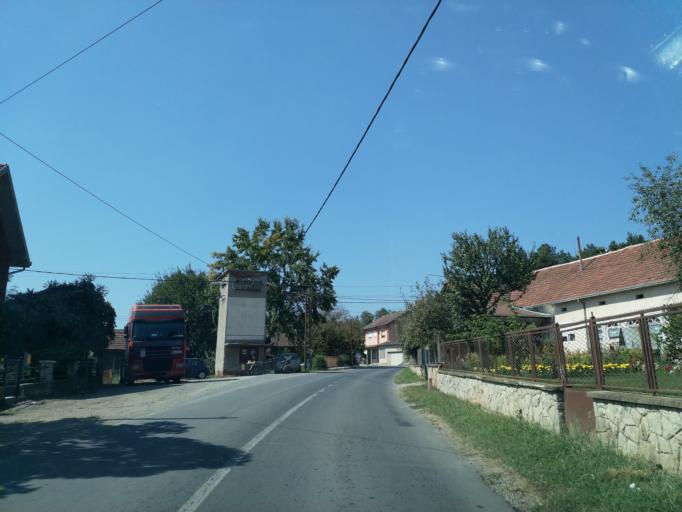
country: RS
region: Central Serbia
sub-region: Rasinski Okrug
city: Krusevac
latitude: 43.6150
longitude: 21.2011
